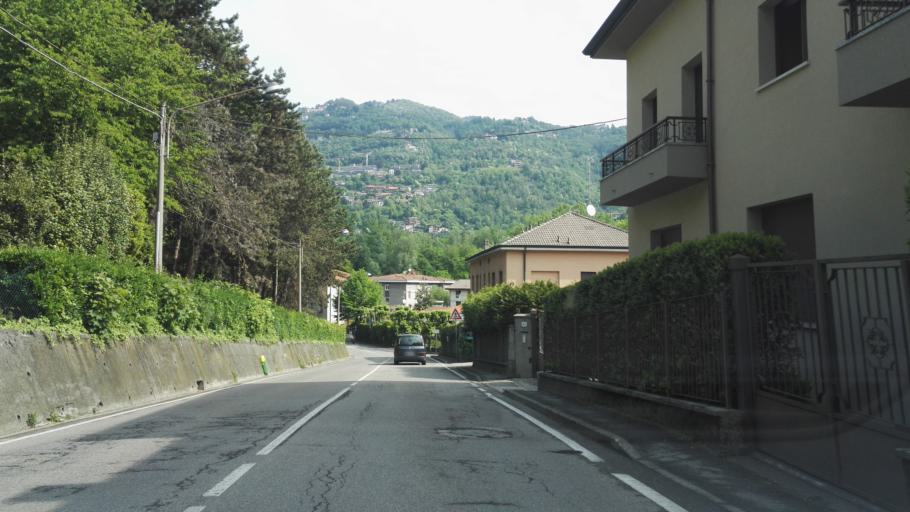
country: IT
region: Lombardy
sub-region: Provincia di Como
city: Como
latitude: 45.7976
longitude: 9.0988
